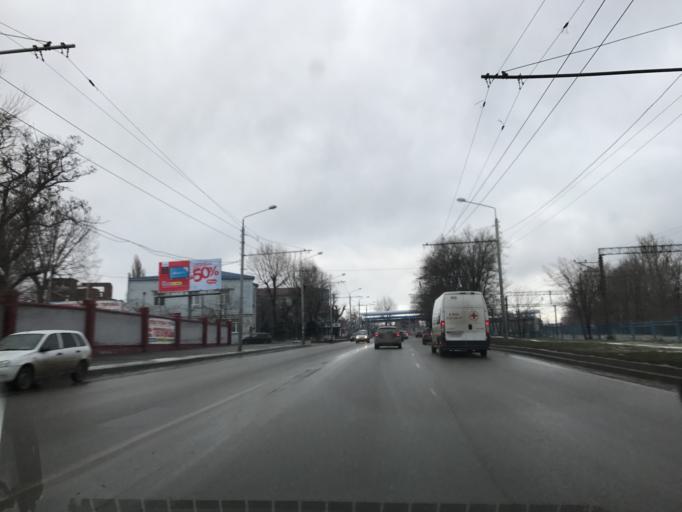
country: RU
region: Rostov
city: Imeni Chkalova
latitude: 47.2597
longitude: 39.7669
